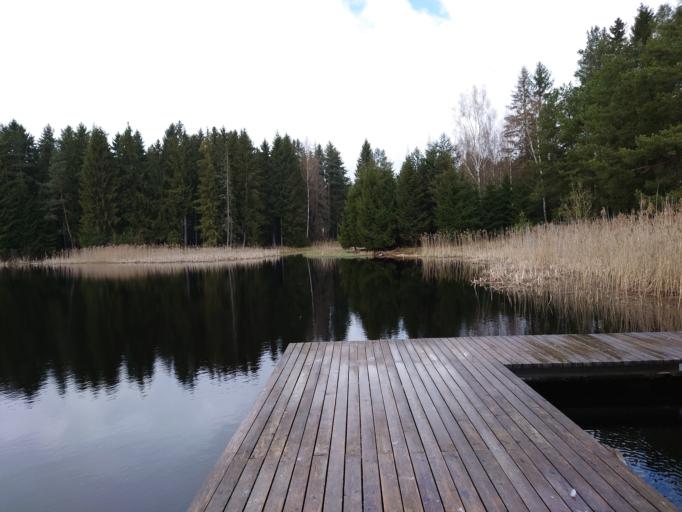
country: EE
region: Vorumaa
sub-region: Voru linn
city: Voru
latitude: 57.9102
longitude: 26.9829
